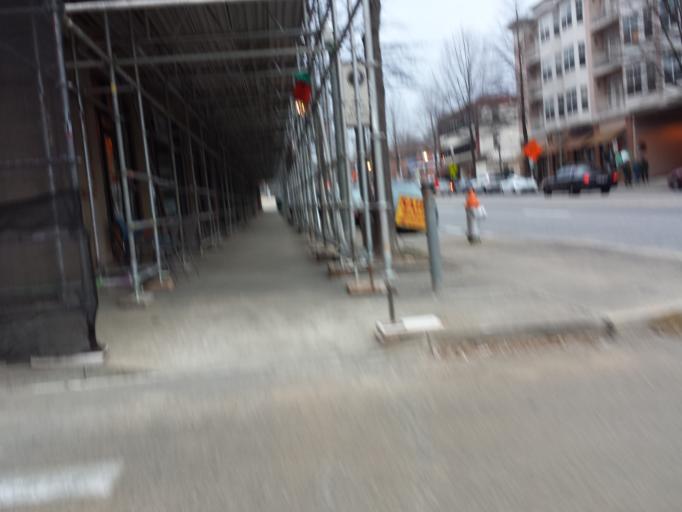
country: US
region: Georgia
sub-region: DeKalb County
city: Decatur
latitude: 33.7757
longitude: -84.2942
